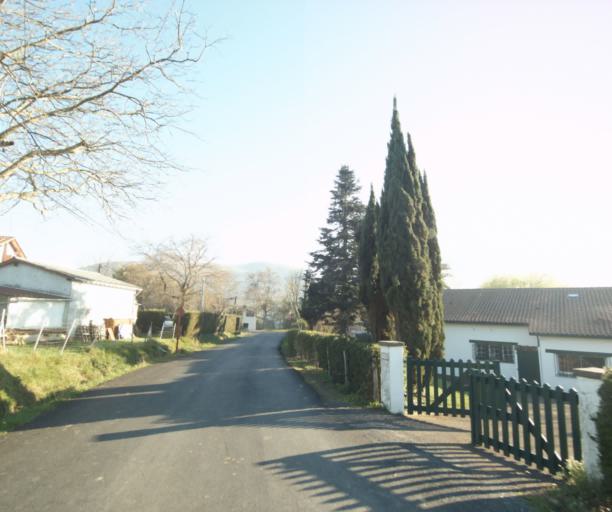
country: FR
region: Aquitaine
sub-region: Departement des Pyrenees-Atlantiques
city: Urrugne
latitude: 43.3431
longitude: -1.7014
